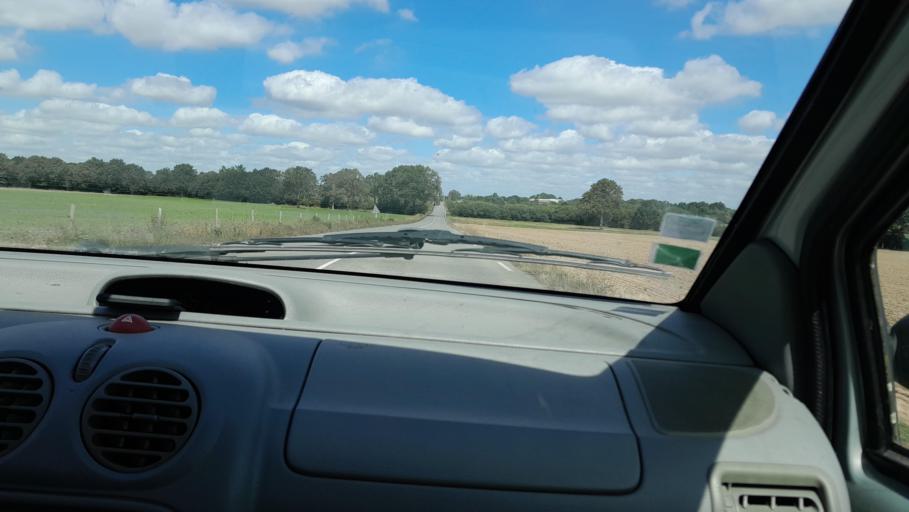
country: FR
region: Pays de la Loire
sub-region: Departement de la Mayenne
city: Ballots
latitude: 47.9148
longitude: -1.0624
